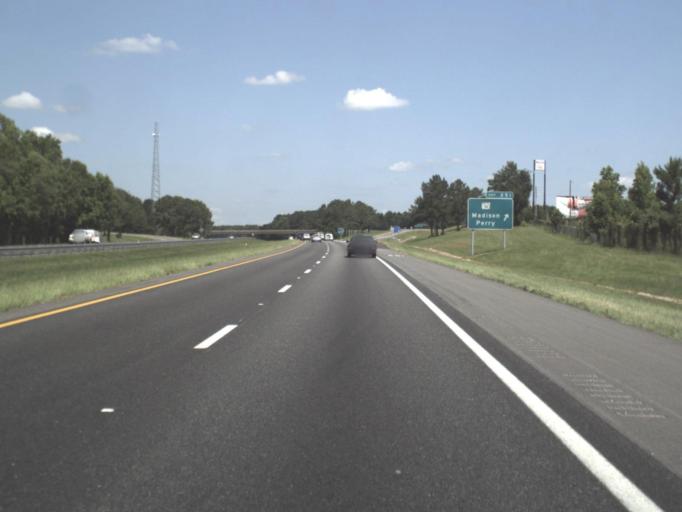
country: US
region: Florida
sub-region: Madison County
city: Madison
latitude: 30.4282
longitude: -83.4507
